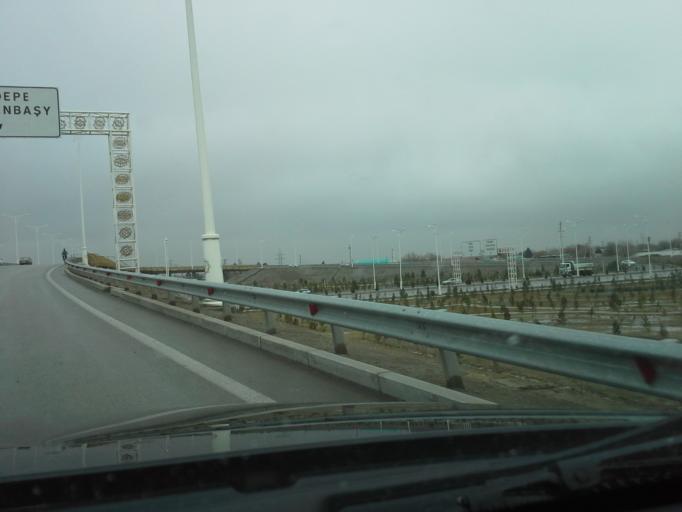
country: TM
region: Ahal
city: Ashgabat
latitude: 37.9492
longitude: 58.4360
